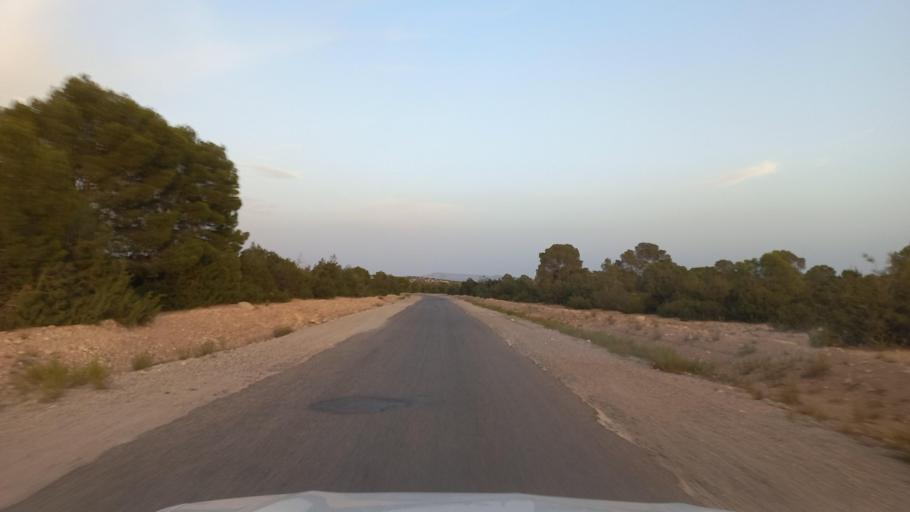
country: TN
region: Al Qasrayn
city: Sbiba
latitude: 35.4136
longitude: 8.9318
